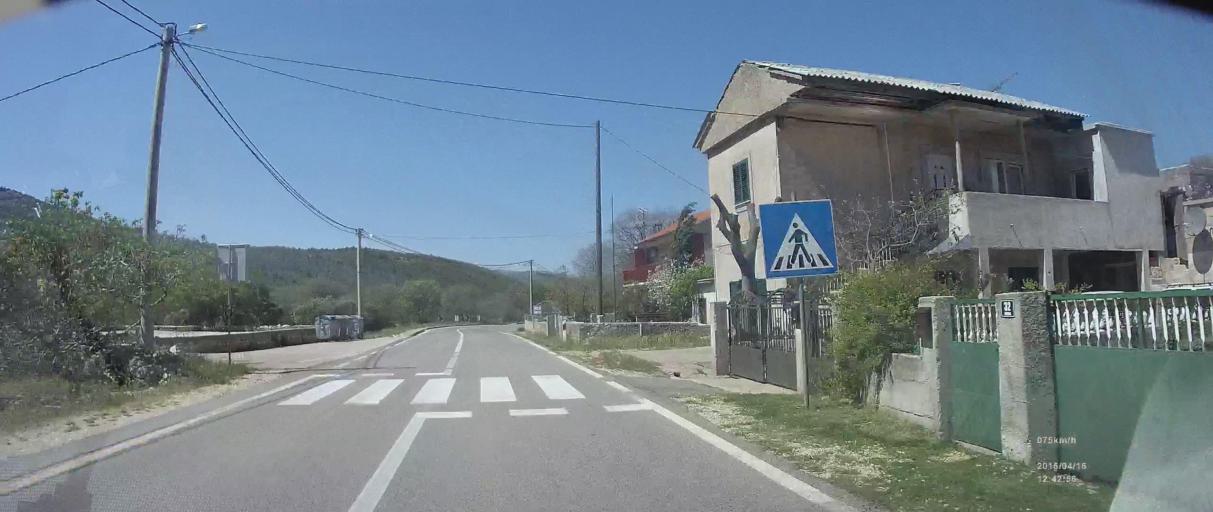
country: HR
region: Sibensko-Kniniska
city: Rogoznica
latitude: 43.6305
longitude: 16.0818
